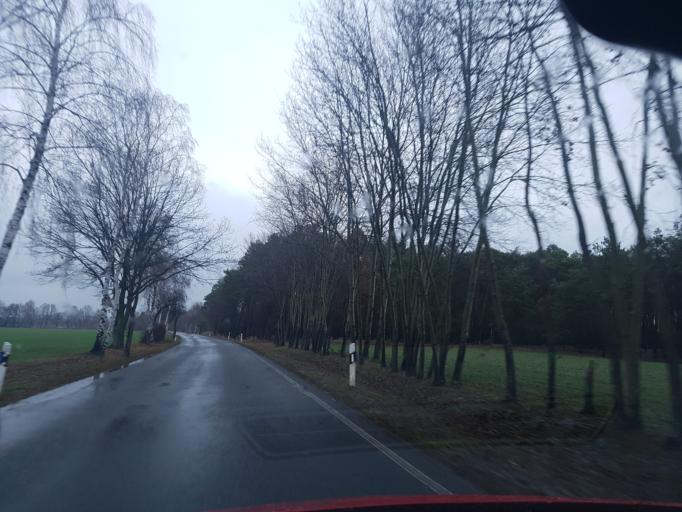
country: DE
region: Brandenburg
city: Schilda
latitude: 51.6197
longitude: 13.3191
